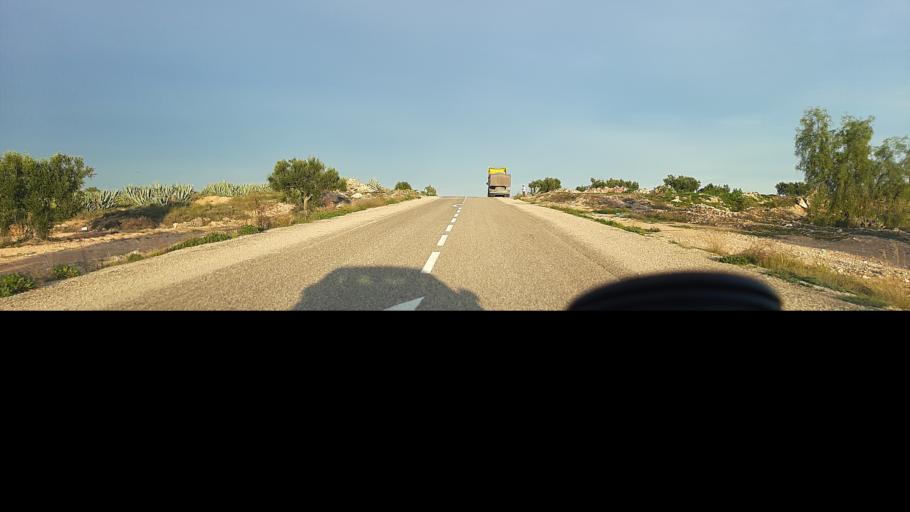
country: TN
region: Safaqis
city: Sfax
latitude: 34.9544
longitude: 10.5546
